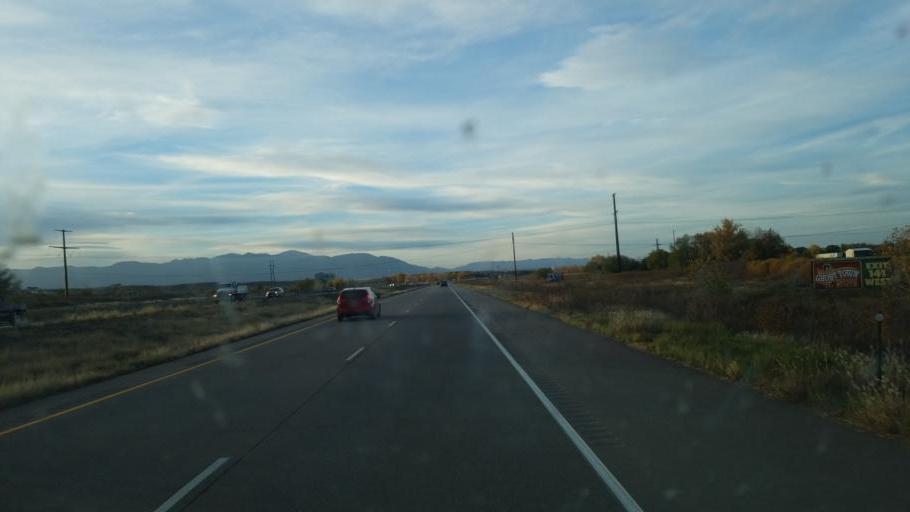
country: US
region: Colorado
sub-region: El Paso County
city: Fountain
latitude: 38.5782
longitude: -104.6625
